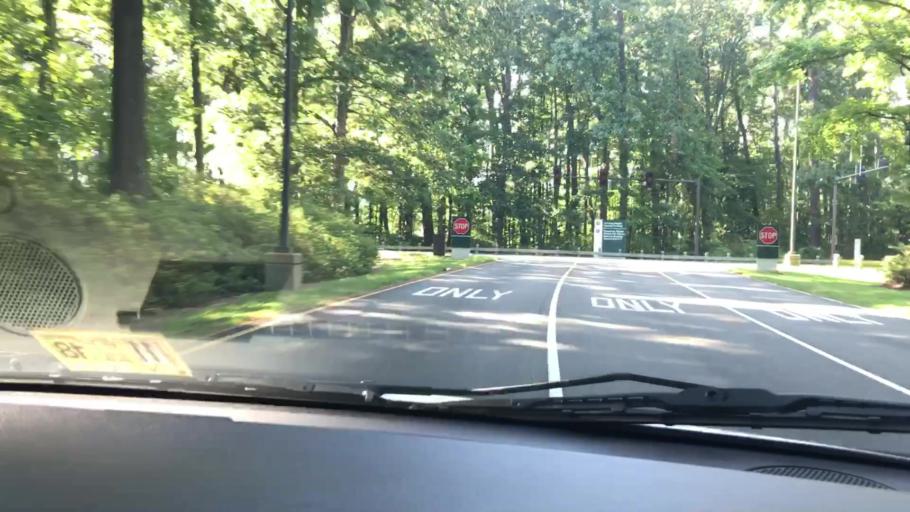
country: US
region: Virginia
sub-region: City of Norfolk
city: Norfolk
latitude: 36.8986
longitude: -76.2098
